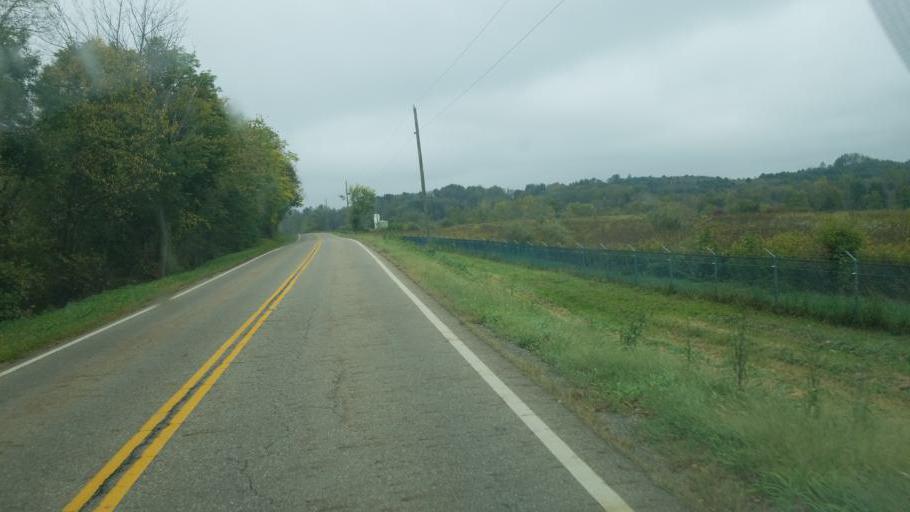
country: US
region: Ohio
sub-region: Carroll County
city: Lake Mohawk
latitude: 40.6280
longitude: -81.2873
